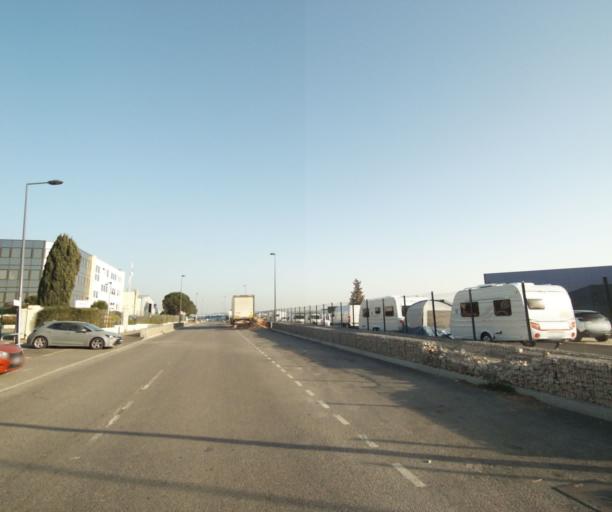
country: FR
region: Provence-Alpes-Cote d'Azur
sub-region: Departement des Bouches-du-Rhone
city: Saint-Victoret
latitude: 43.4328
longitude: 5.2463
